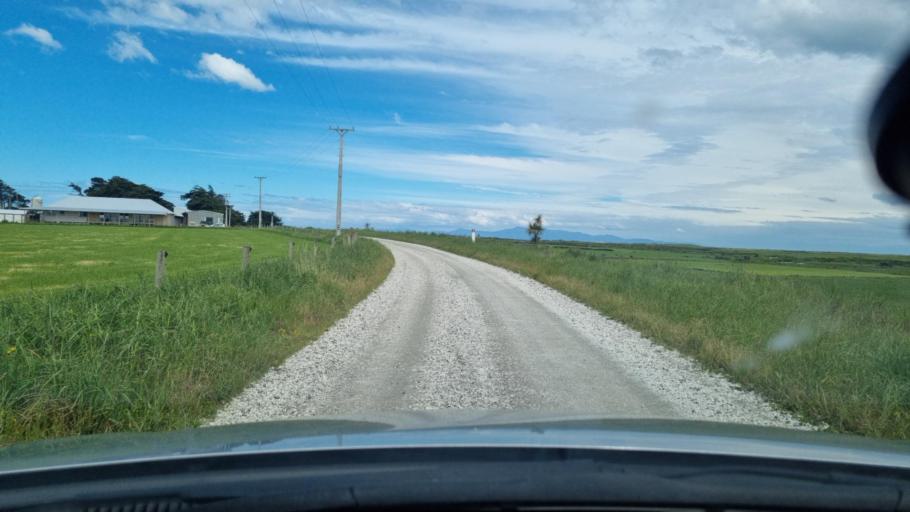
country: NZ
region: Southland
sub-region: Invercargill City
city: Invercargill
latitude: -46.3989
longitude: 168.2566
